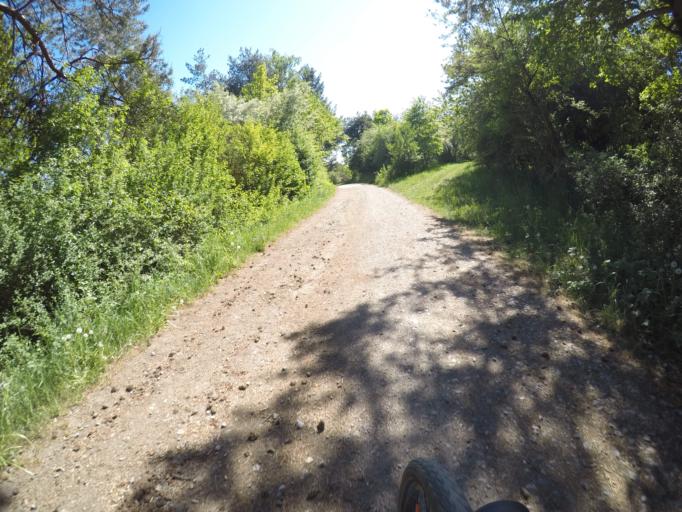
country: DE
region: Baden-Wuerttemberg
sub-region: Regierungsbezirk Stuttgart
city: Weissach
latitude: 48.8321
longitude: 8.8998
